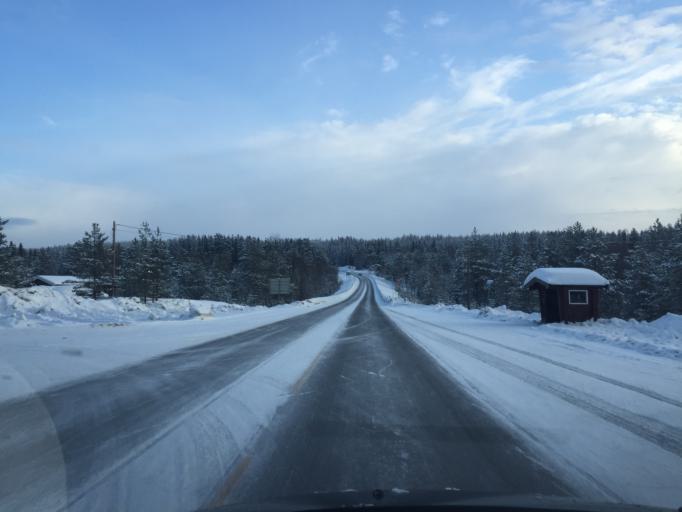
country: NO
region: Hedmark
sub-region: Trysil
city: Innbygda
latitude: 61.0872
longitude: 11.9905
